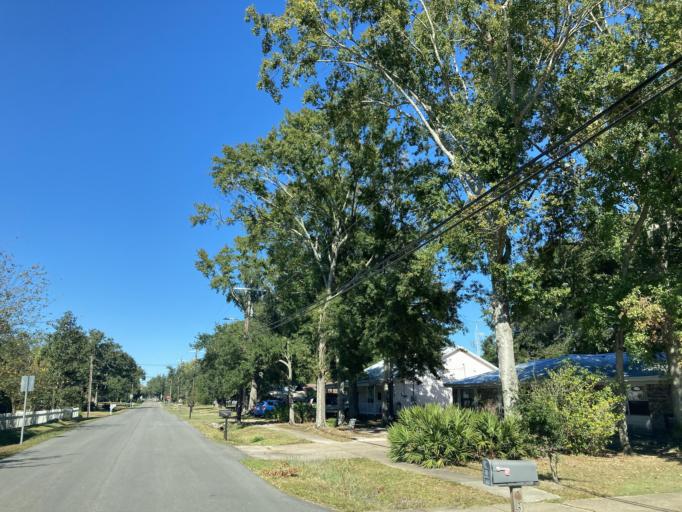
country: US
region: Mississippi
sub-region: Jackson County
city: Ocean Springs
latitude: 30.4053
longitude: -88.8102
